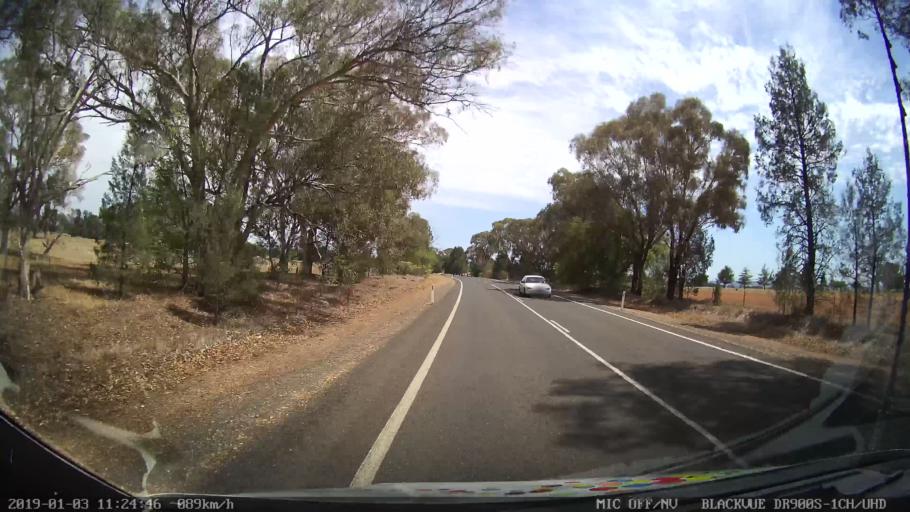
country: AU
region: New South Wales
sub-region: Weddin
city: Grenfell
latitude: -34.0472
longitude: 148.2330
